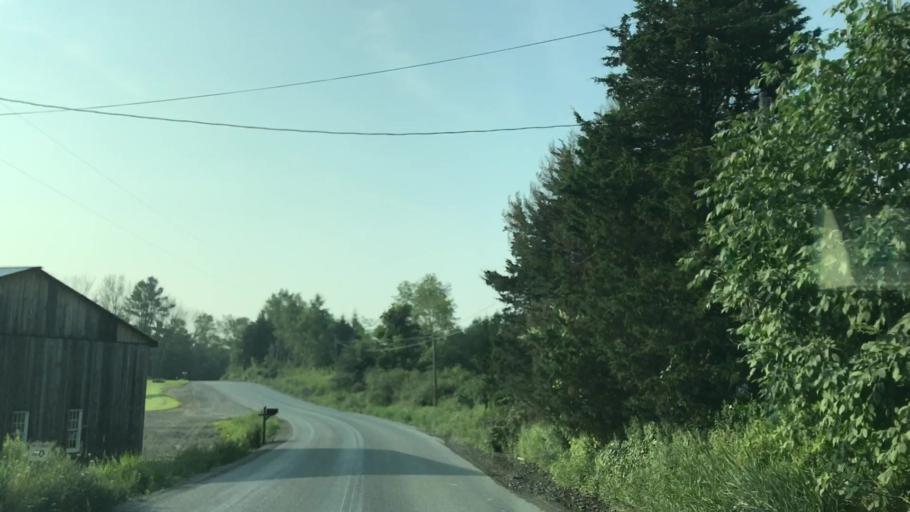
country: US
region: Pennsylvania
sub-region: Wyoming County
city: Factoryville
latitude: 41.6709
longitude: -75.8134
